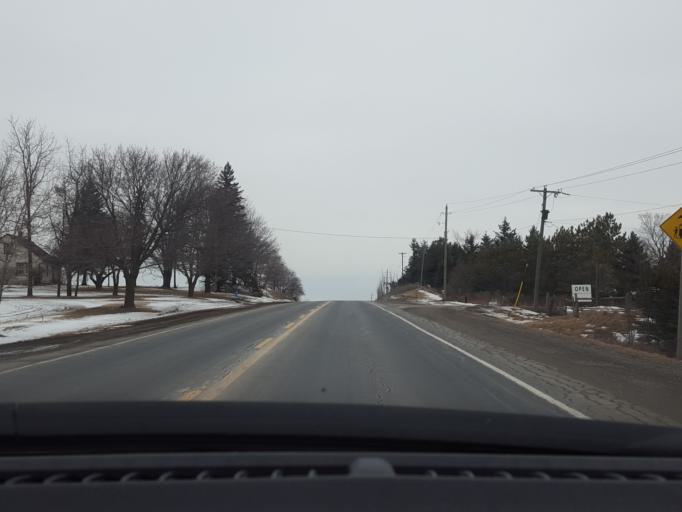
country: CA
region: Ontario
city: Newmarket
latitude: 44.1298
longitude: -79.4224
